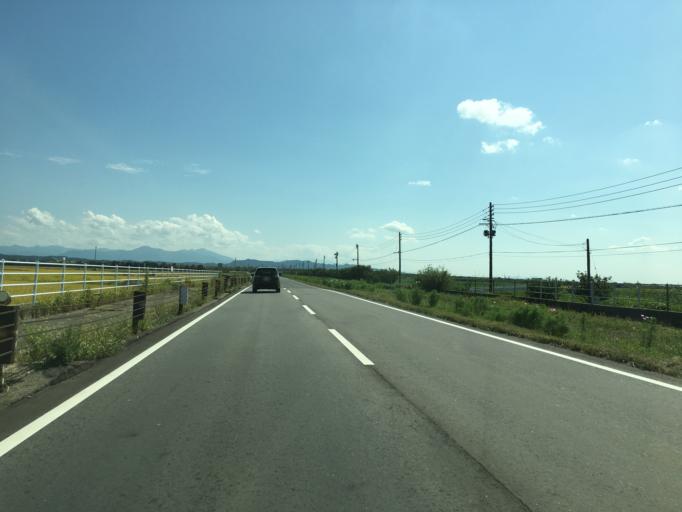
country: JP
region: Niigata
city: Niitsu-honcho
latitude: 37.8287
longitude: 139.0976
